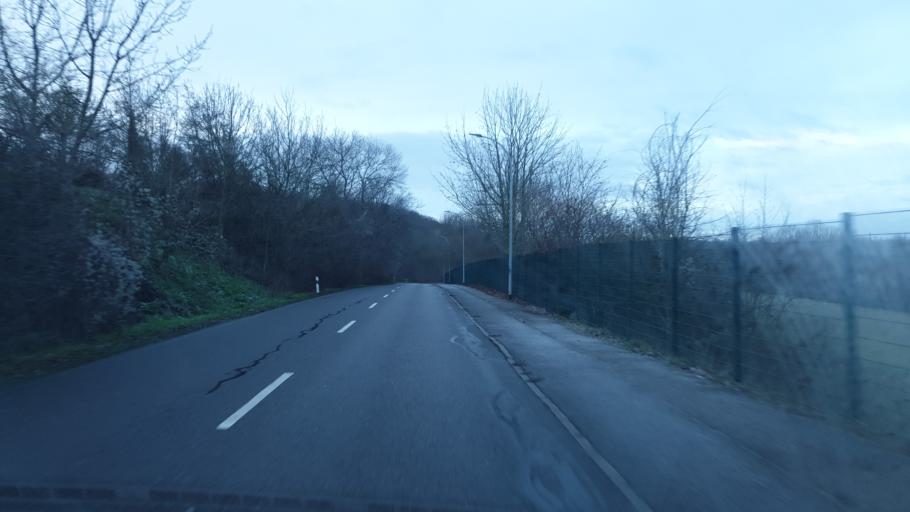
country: DE
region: Saxony-Anhalt
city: Burgwerben
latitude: 51.2113
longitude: 11.9851
